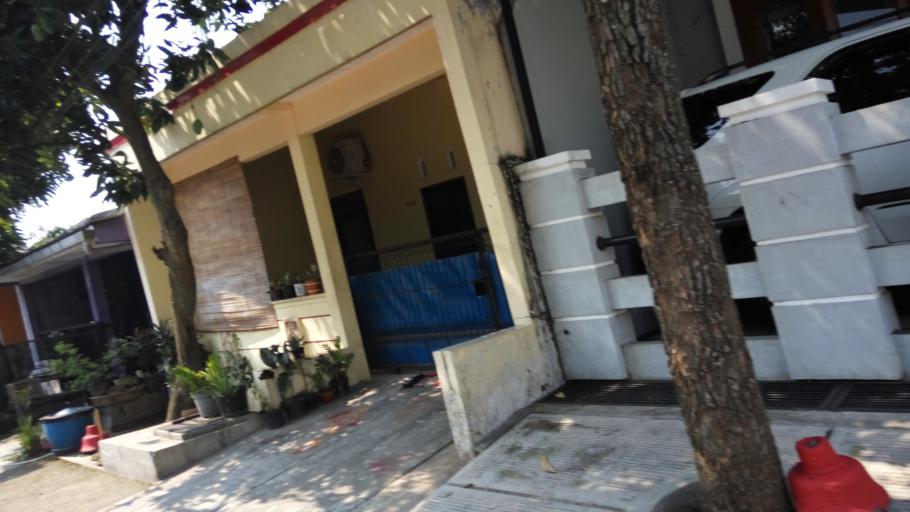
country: ID
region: Central Java
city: Mranggen
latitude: -7.0342
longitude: 110.4740
